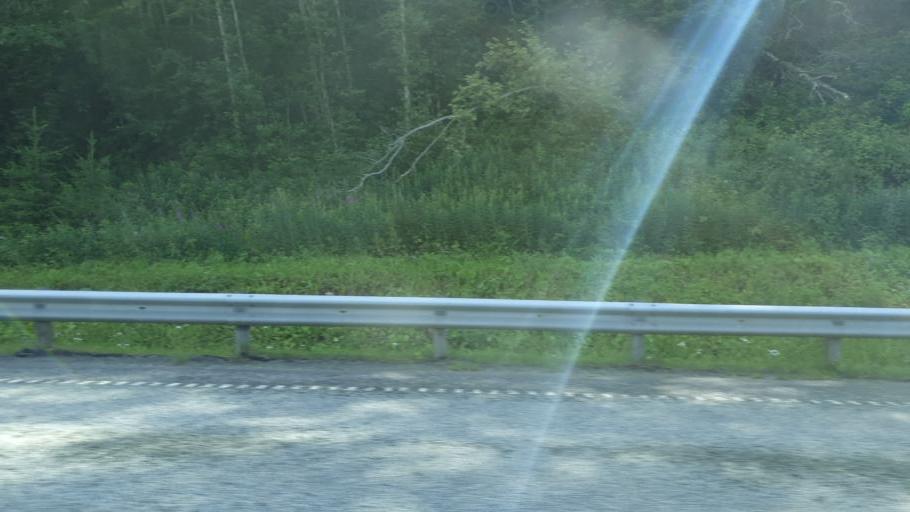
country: NO
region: Sor-Trondelag
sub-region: Midtre Gauldal
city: Storen
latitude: 63.0424
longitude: 10.2993
